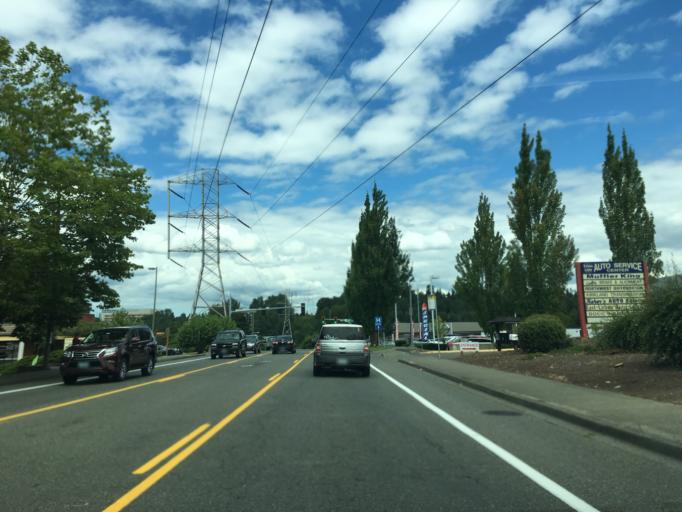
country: US
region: Washington
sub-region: King County
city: Kingsgate
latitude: 47.7067
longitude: -122.1757
